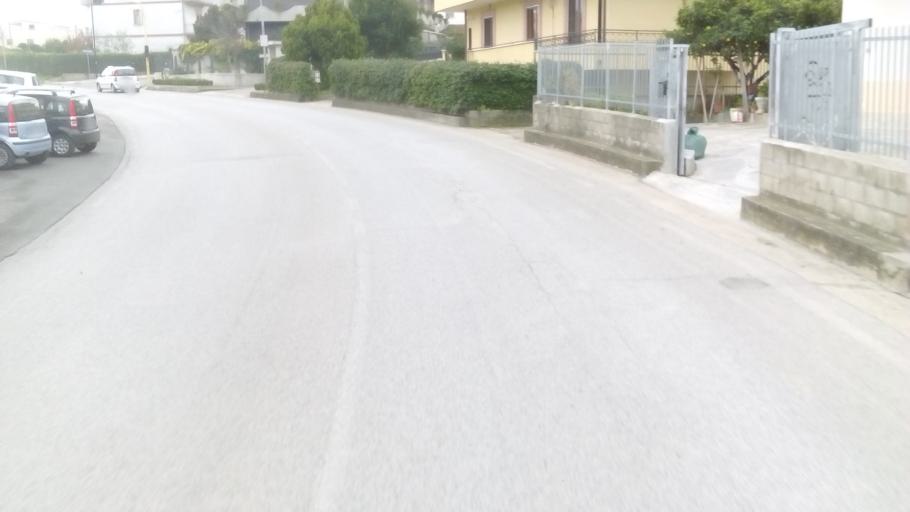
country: IT
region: Abruzzo
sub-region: Provincia di Chieti
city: Vasto
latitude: 42.0978
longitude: 14.6965
